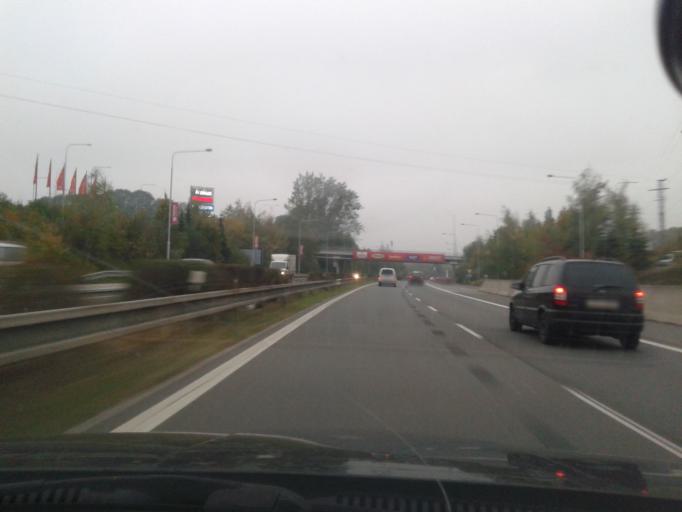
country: CZ
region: Moravskoslezsky
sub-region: Okres Ostrava-Mesto
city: Ostrava
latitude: 49.7980
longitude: 18.2261
